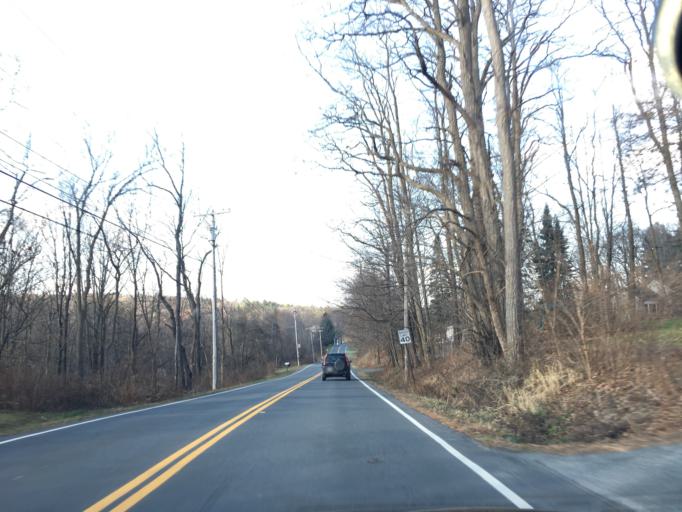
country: US
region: New York
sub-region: Rensselaer County
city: West Sand Lake
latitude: 42.6190
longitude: -73.6500
